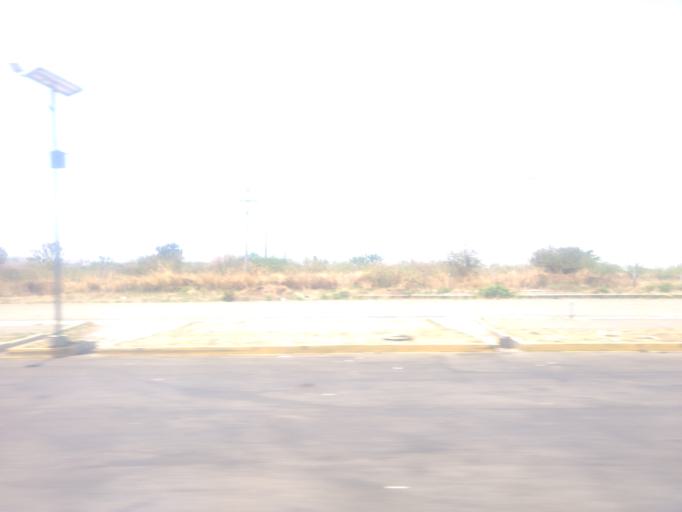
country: MX
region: Jalisco
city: Tonila
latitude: 19.4101
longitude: -103.5266
